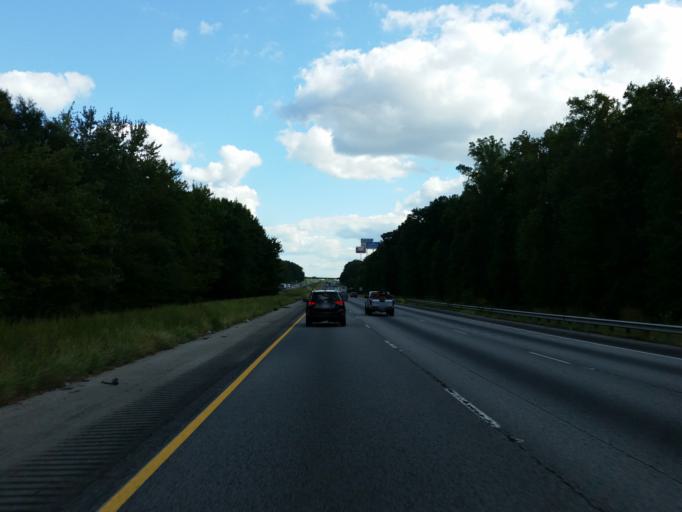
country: US
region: Georgia
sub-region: Henry County
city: Locust Grove
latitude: 33.3859
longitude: -84.1435
